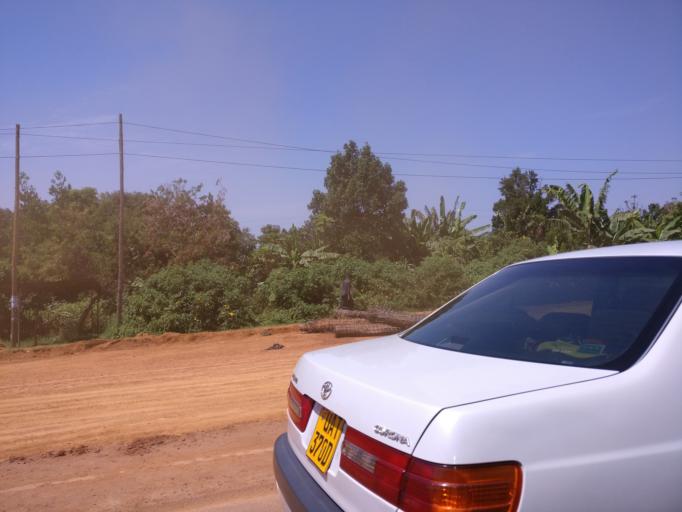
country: UG
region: Central Region
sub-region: Wakiso District
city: Entebbe
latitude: 0.0736
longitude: 32.4776
